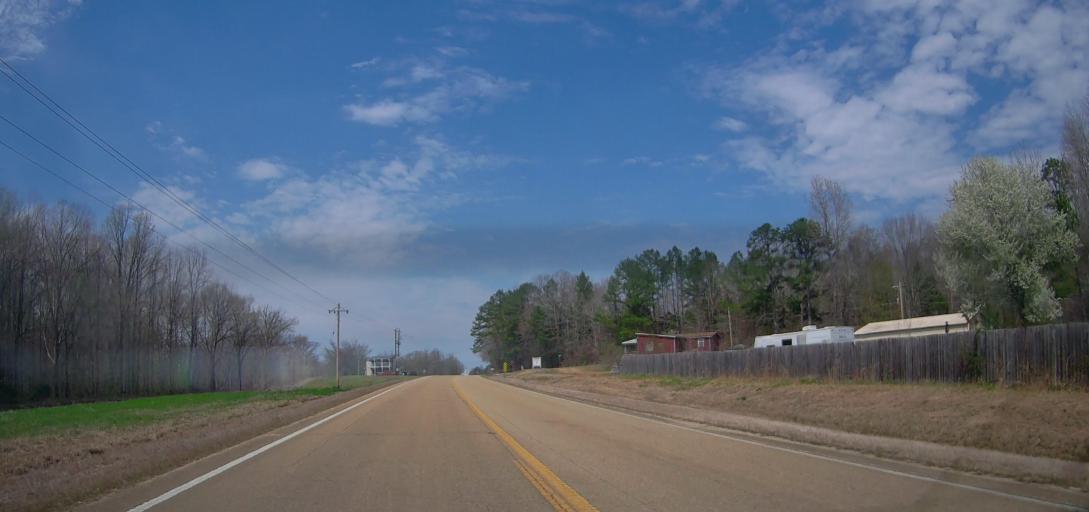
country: US
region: Mississippi
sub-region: Benton County
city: Ashland
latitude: 34.6300
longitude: -89.2701
